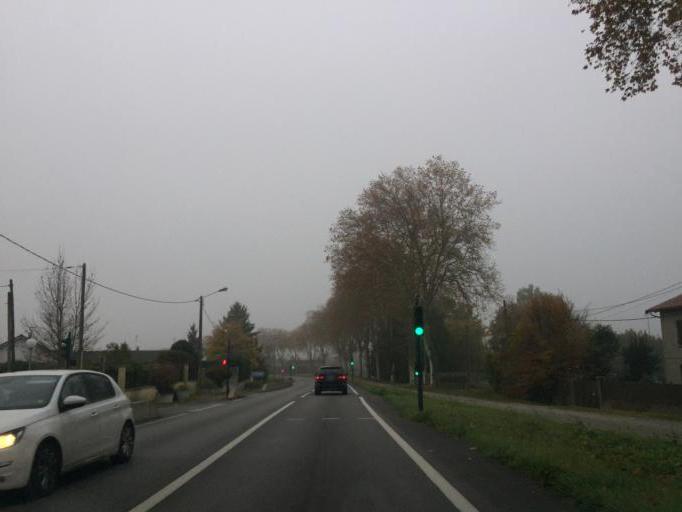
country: FR
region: Rhone-Alpes
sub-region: Departement de l'Ain
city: Mionnay
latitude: 45.9014
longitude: 4.9331
